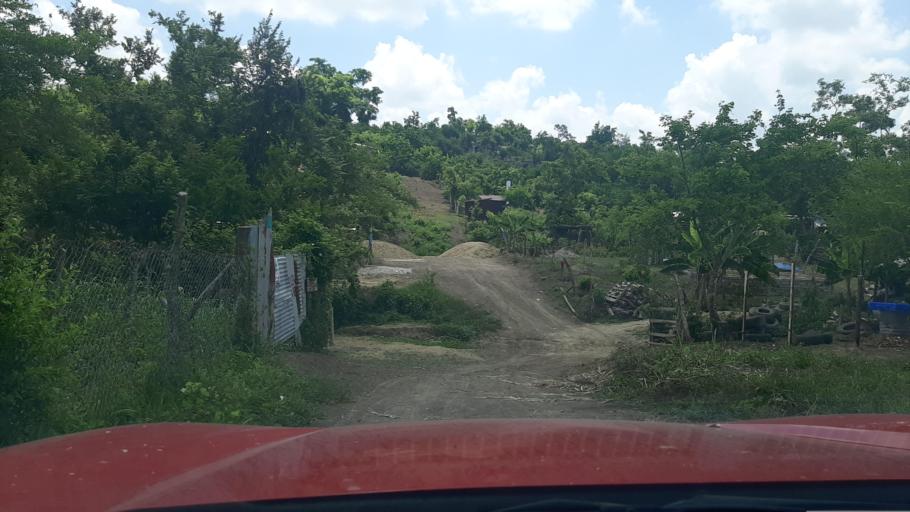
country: MX
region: Veracruz
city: Coatzintla
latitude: 20.5049
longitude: -97.4593
